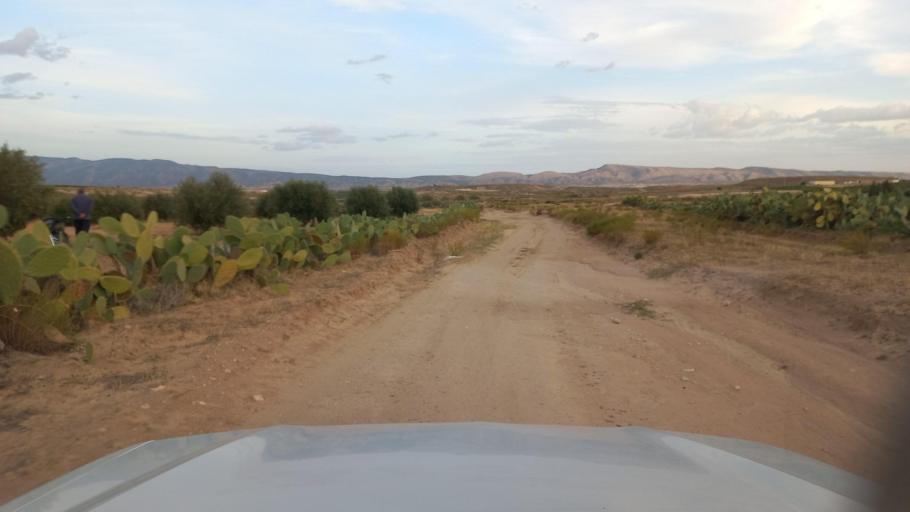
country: TN
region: Al Qasrayn
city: Sbiba
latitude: 35.4112
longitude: 9.0826
